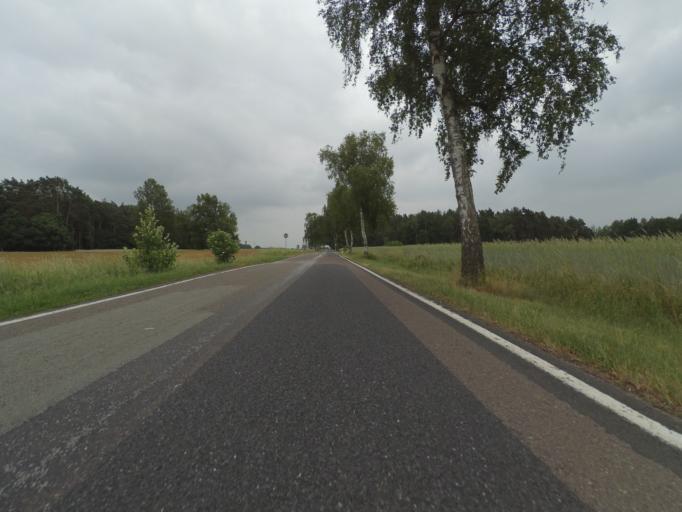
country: DE
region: Mecklenburg-Vorpommern
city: Siggelkow
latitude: 53.3759
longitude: 11.9889
